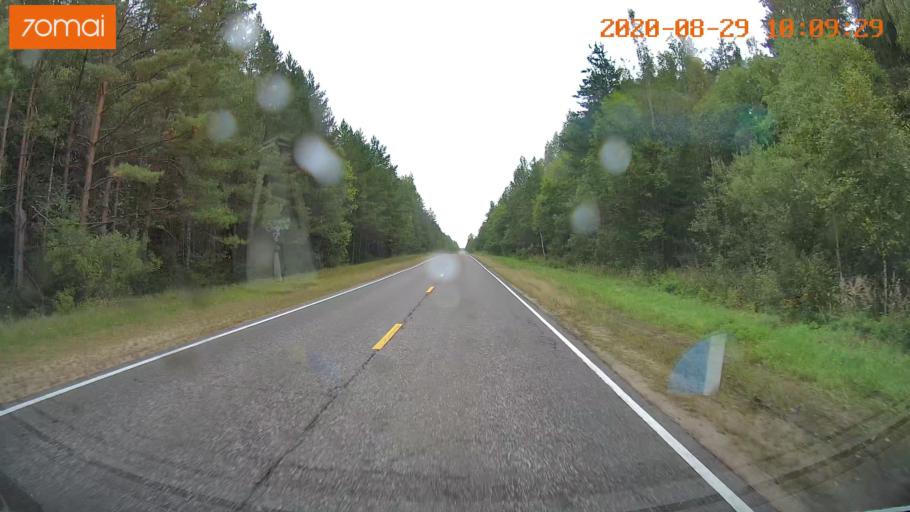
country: RU
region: Ivanovo
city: Kuznechikha
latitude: 57.3752
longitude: 42.6271
